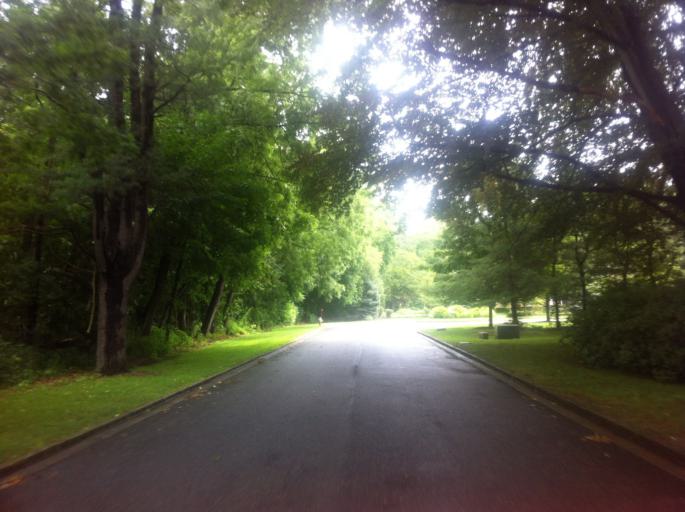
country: US
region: New York
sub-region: Nassau County
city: Muttontown
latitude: 40.8254
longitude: -73.5602
